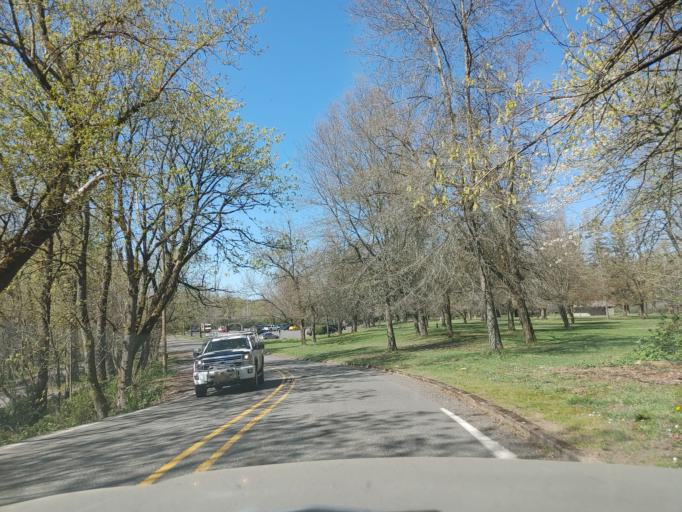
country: US
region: Oregon
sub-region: Multnomah County
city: Troutdale
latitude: 45.5403
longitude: -122.3790
